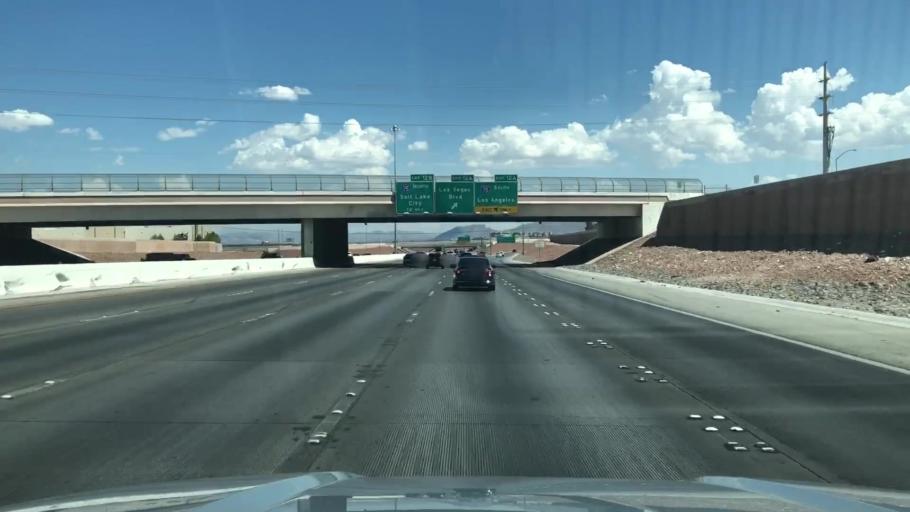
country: US
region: Nevada
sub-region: Clark County
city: Paradise
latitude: 36.0666
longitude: -115.1912
